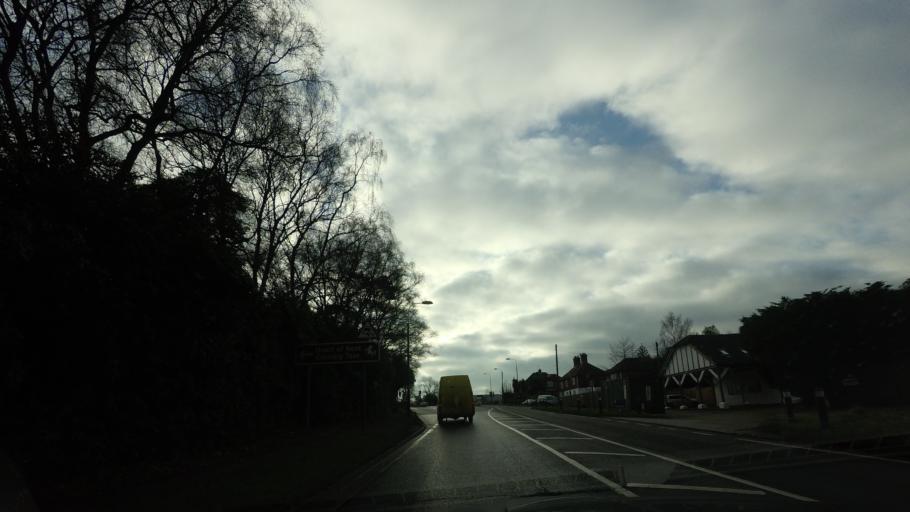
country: GB
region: England
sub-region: Kent
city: Hawkhurst
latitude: 51.0553
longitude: 0.4463
